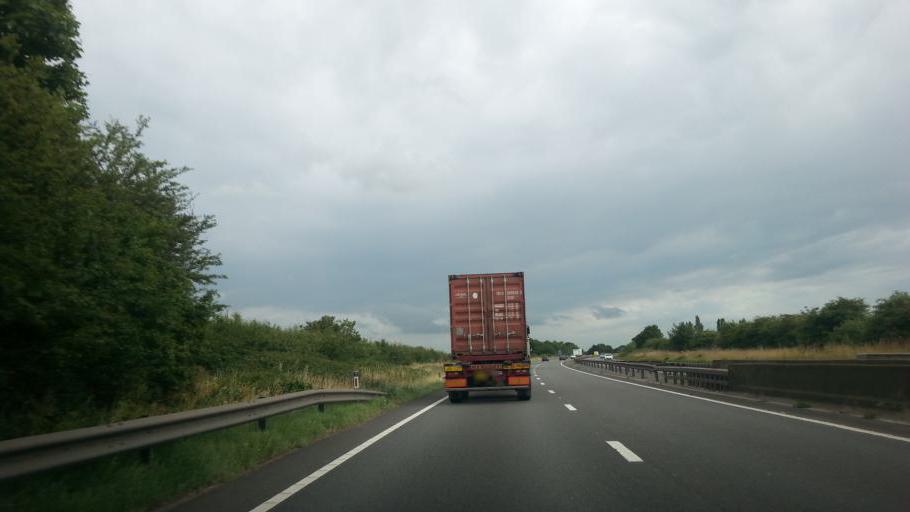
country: GB
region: England
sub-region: Nottinghamshire
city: Newark on Trent
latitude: 53.0640
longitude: -0.7651
